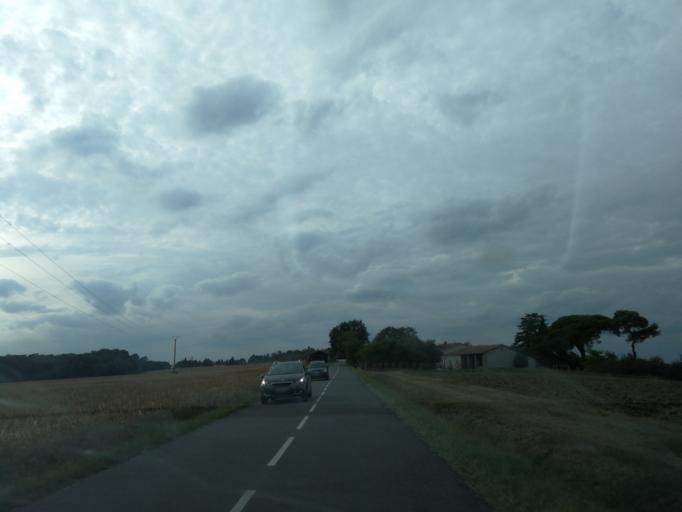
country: FR
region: Midi-Pyrenees
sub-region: Departement de la Haute-Garonne
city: Flourens
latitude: 43.6078
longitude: 1.5410
